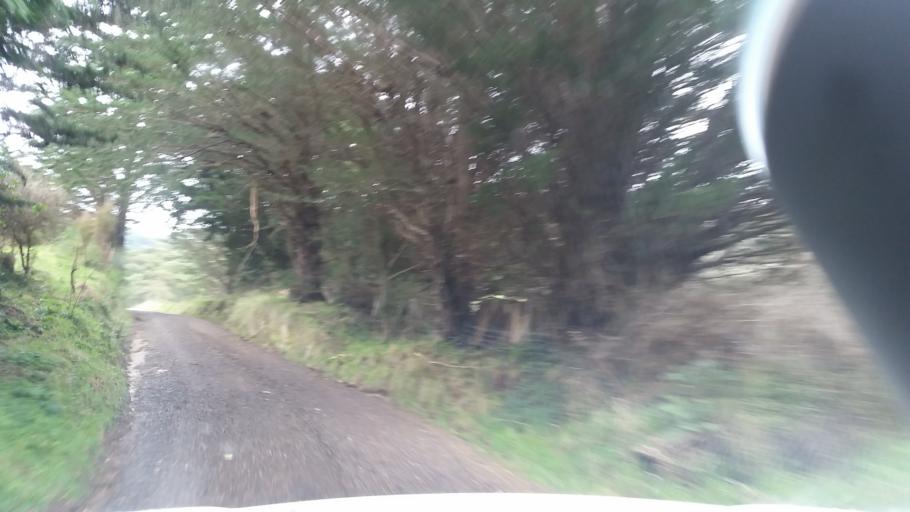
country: NZ
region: Canterbury
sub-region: Christchurch City
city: Christchurch
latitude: -43.7509
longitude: 173.0364
